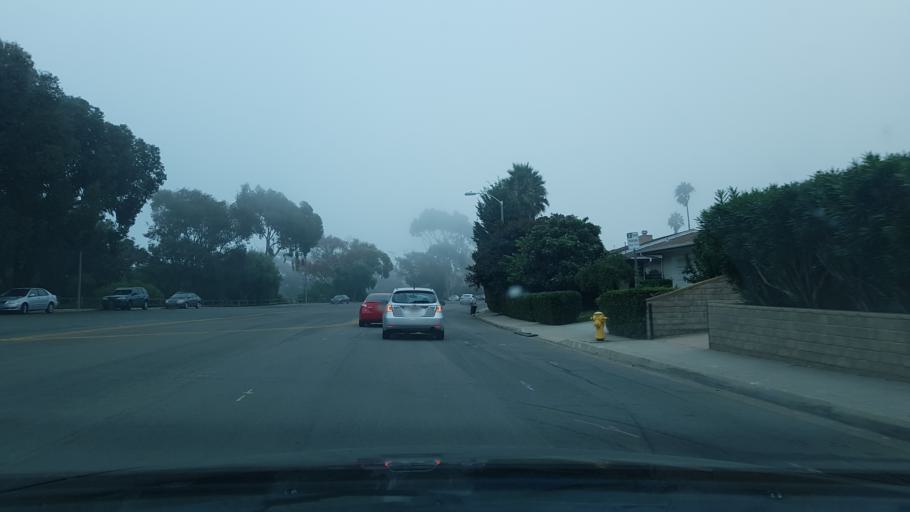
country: US
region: California
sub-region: San Diego County
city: La Jolla
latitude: 32.8680
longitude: -117.2401
